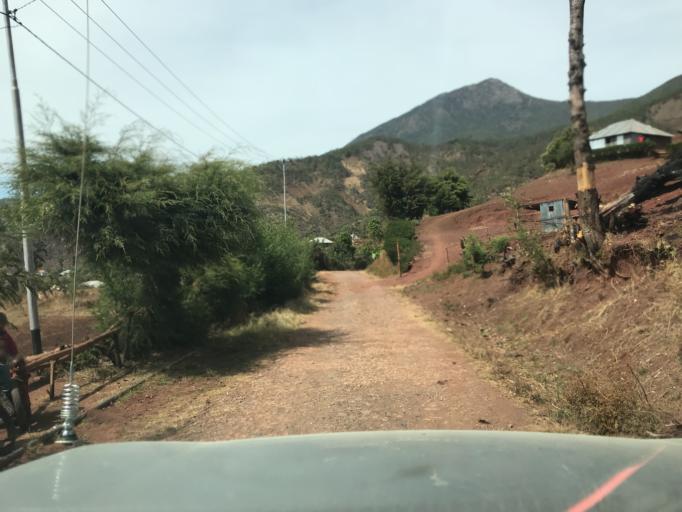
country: TL
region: Ainaro
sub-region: Ainaro
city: Ainaro
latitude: -8.8867
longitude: 125.5205
